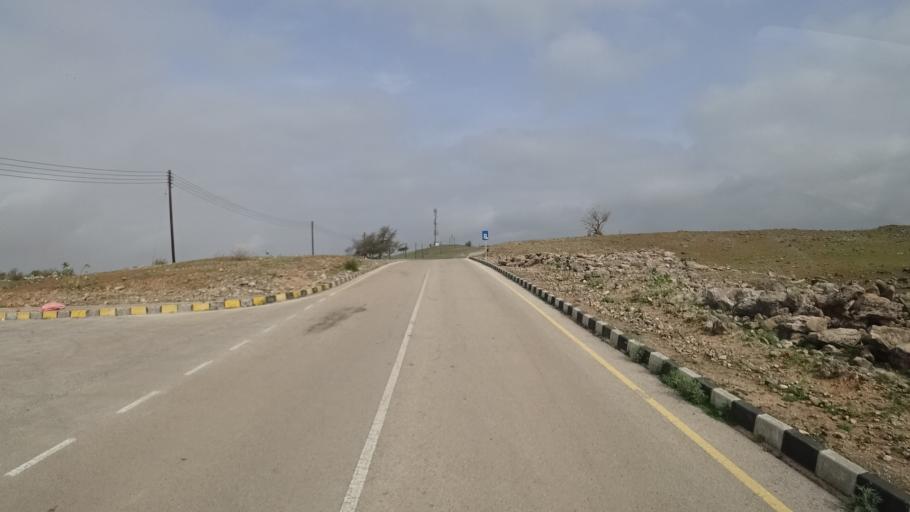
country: OM
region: Zufar
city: Salalah
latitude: 17.0775
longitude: 54.4490
